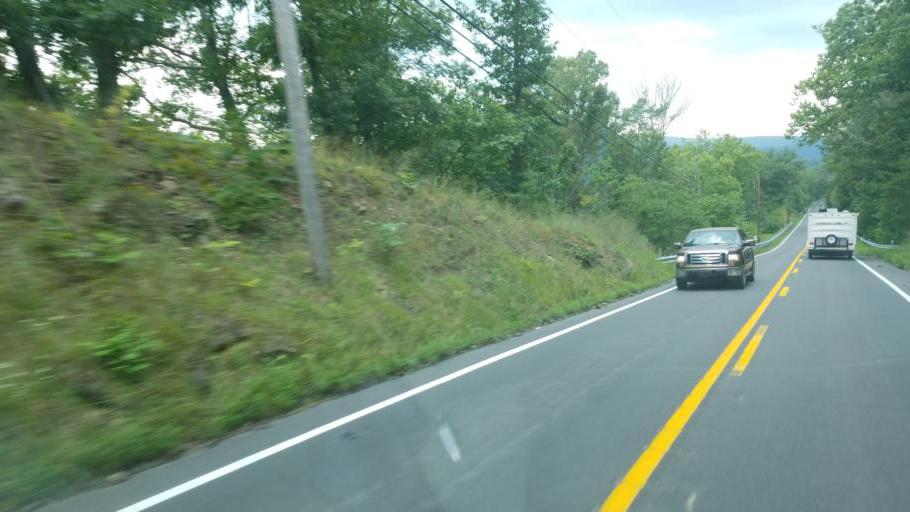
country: US
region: West Virginia
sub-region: Mineral County
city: Fort Ashby
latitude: 39.5270
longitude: -78.5220
